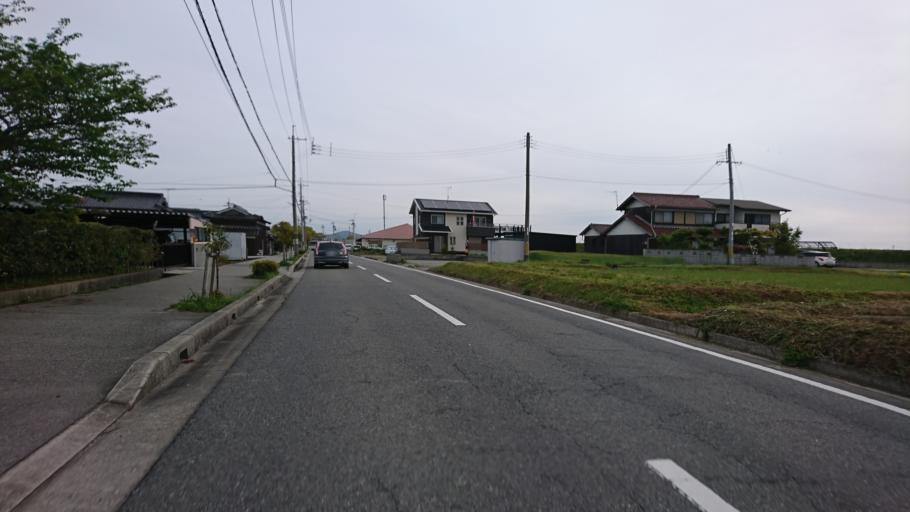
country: JP
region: Hyogo
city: Kakogawacho-honmachi
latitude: 34.7675
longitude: 134.9084
